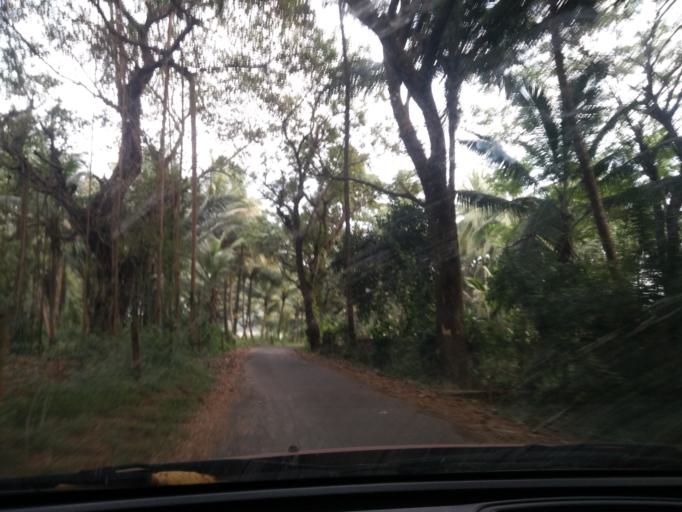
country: IN
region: Goa
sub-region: South Goa
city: Varca
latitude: 15.2229
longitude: 73.9543
